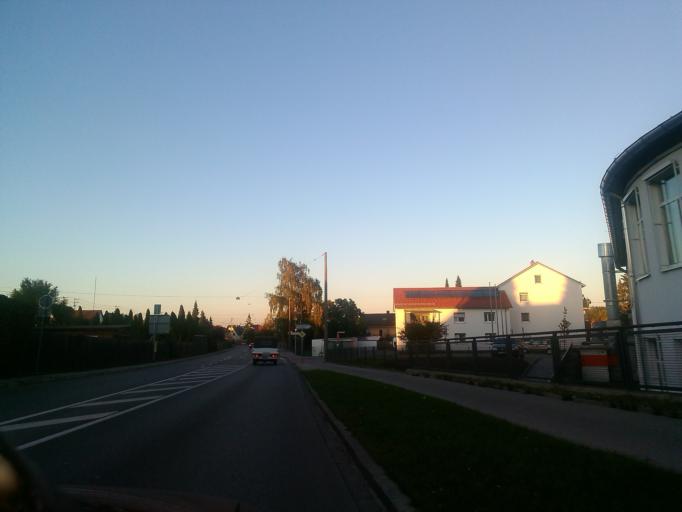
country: DE
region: Bavaria
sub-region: Swabia
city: Friedberg
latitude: 48.3638
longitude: 10.9890
